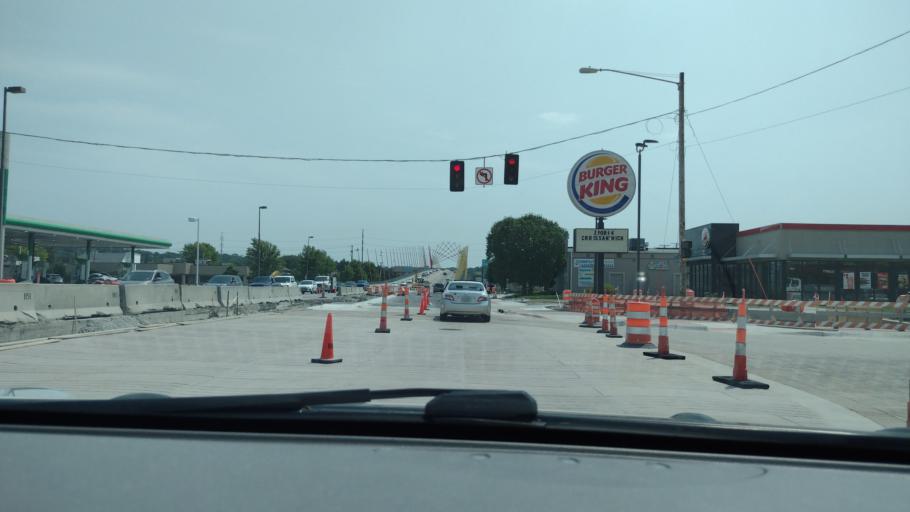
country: US
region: Iowa
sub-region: Pottawattamie County
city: Council Bluffs
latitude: 41.2618
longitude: -95.8677
